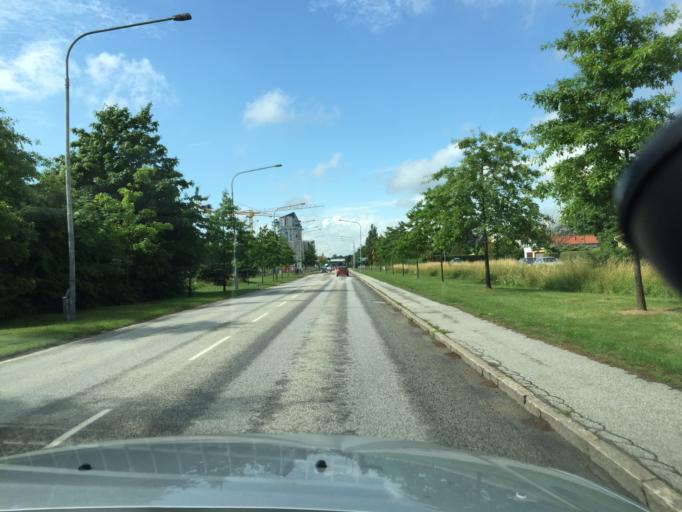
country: SE
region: Skane
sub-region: Lunds Kommun
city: Lund
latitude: 55.6928
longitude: 13.1848
